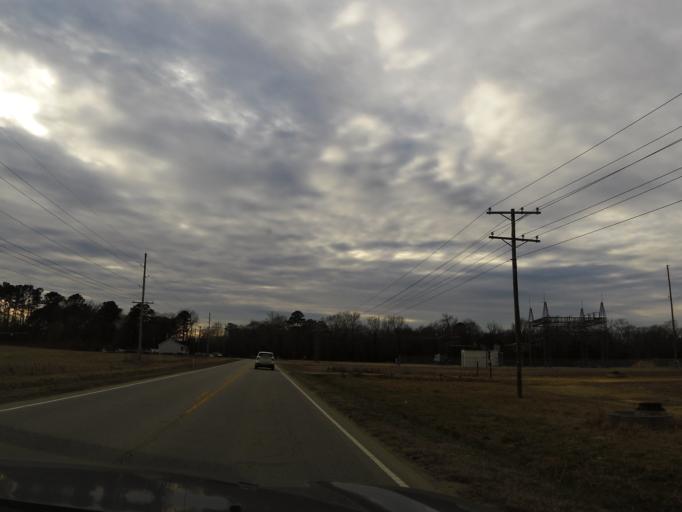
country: US
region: North Carolina
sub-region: Nash County
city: Rocky Mount
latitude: 35.9780
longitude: -77.7632
